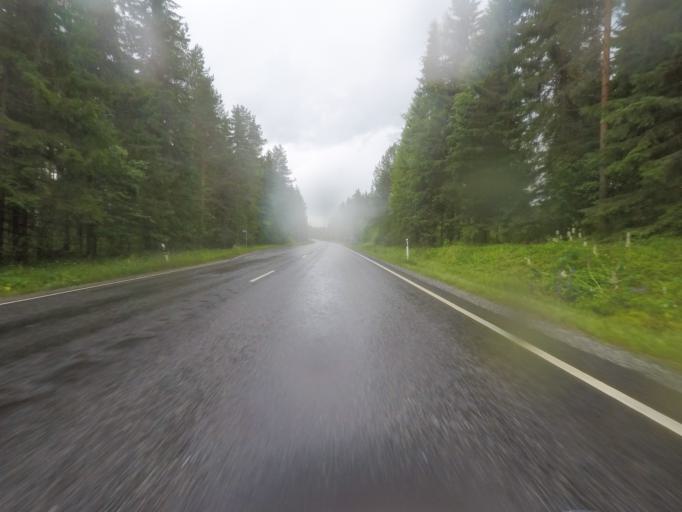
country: FI
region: Central Finland
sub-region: Jyvaeskylae
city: Toivakka
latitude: 62.2011
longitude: 26.2140
